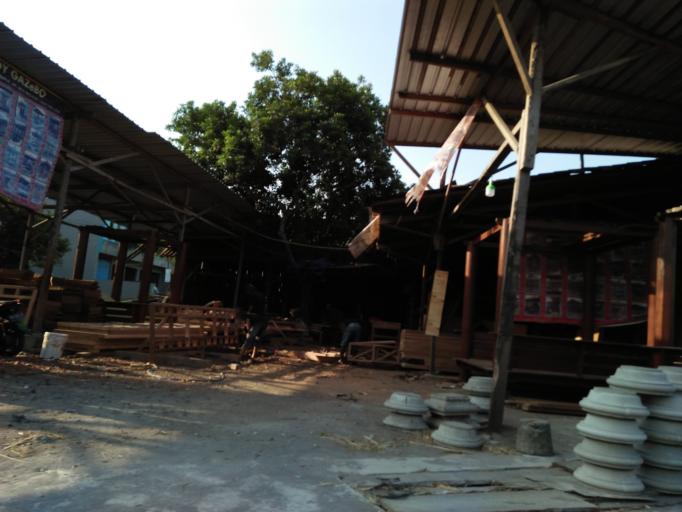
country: ID
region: Daerah Istimewa Yogyakarta
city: Depok
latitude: -7.7778
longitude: 110.4576
